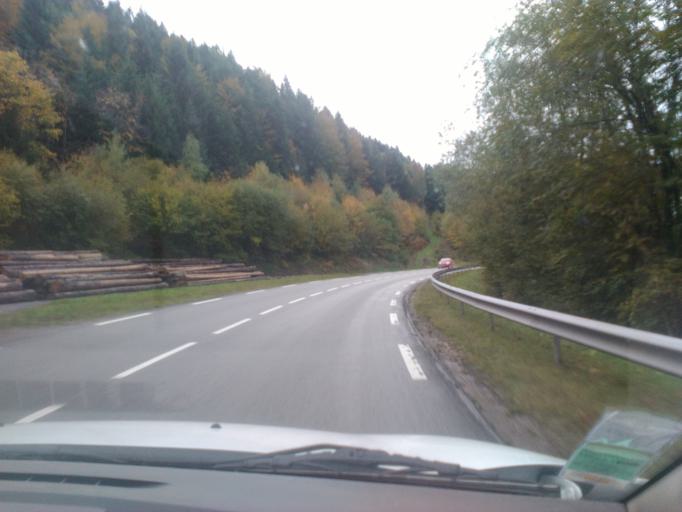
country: FR
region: Lorraine
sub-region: Departement des Vosges
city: Xonrupt-Longemer
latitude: 48.1306
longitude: 6.9165
